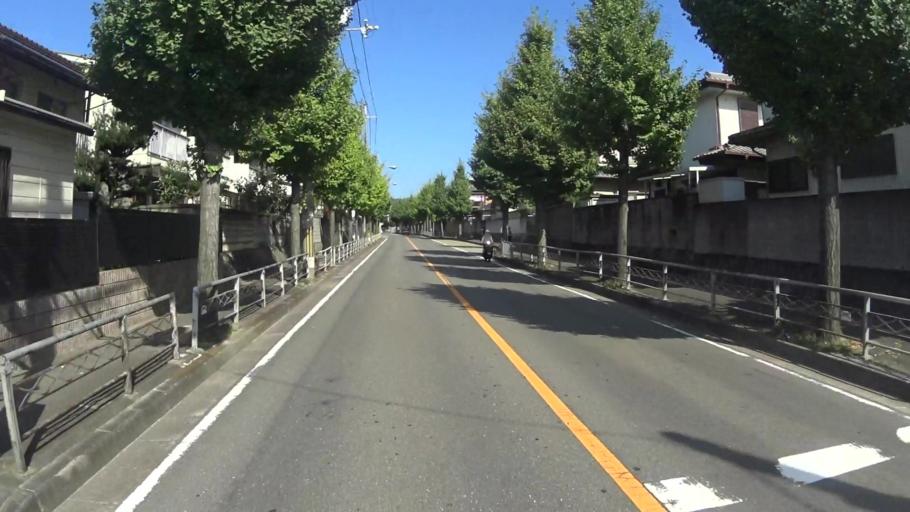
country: JP
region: Kyoto
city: Muko
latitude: 34.9582
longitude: 135.6861
